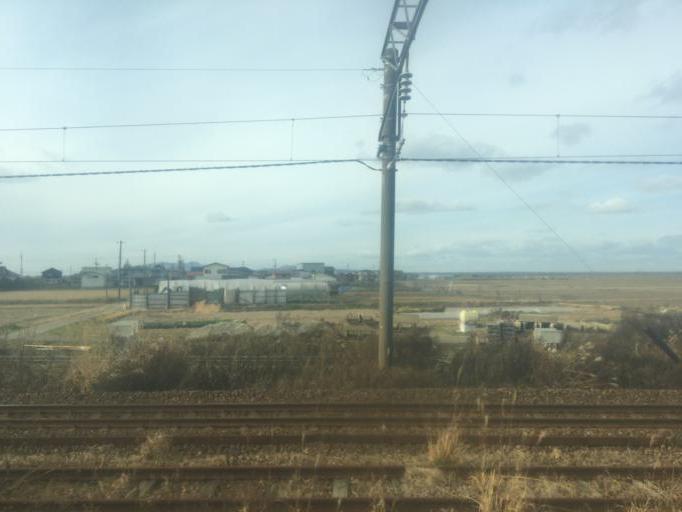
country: JP
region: Akita
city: Tenno
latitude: 39.9002
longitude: 140.0738
